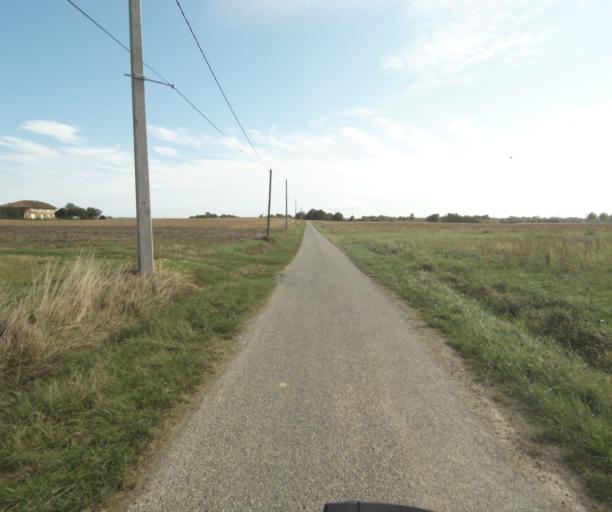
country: FR
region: Midi-Pyrenees
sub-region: Departement du Tarn-et-Garonne
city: Verdun-sur-Garonne
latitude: 43.8467
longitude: 1.1832
